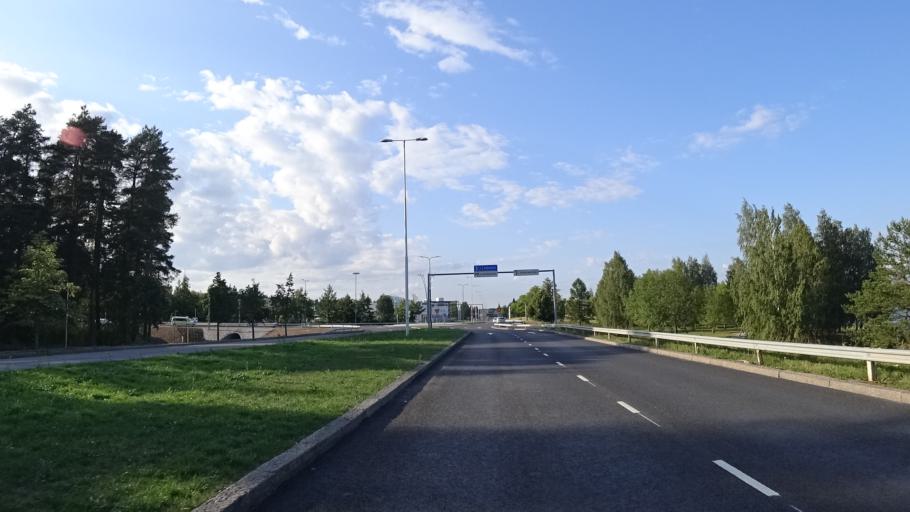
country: FI
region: South Karelia
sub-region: Imatra
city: Imatra
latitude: 61.1877
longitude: 28.7777
